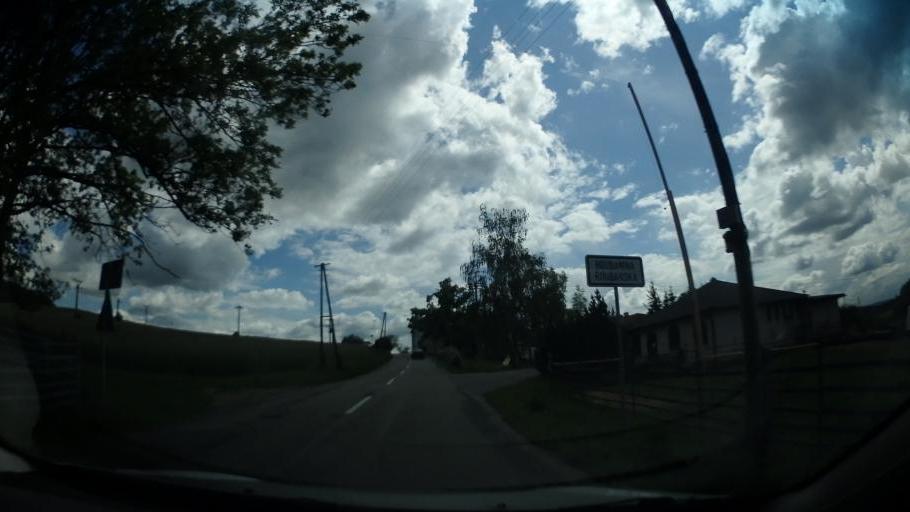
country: CZ
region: South Moravian
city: Velke Opatovice
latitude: 49.6160
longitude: 16.6091
